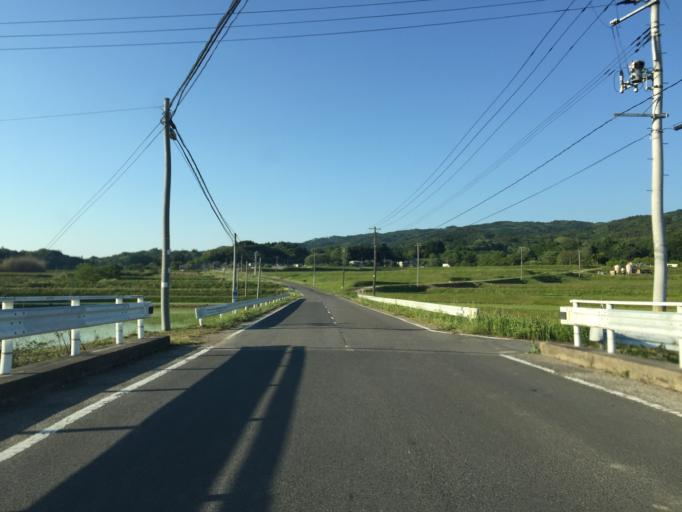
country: JP
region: Fukushima
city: Ishikawa
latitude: 36.9779
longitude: 140.4334
